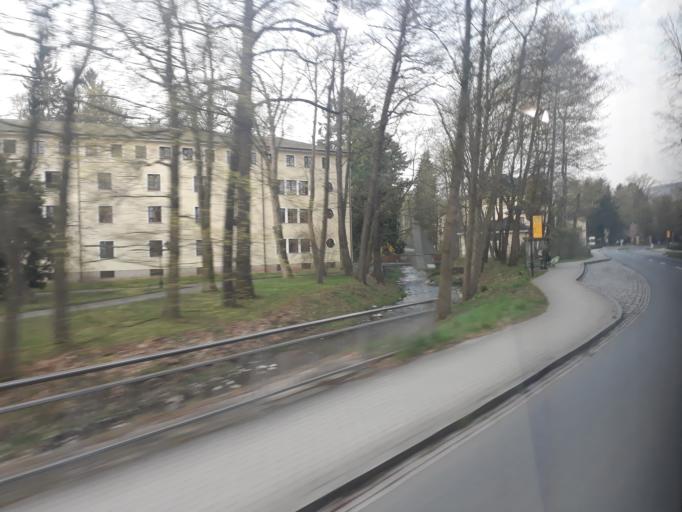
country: DE
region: Saxony
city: Kreischa
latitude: 50.9481
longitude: 13.7657
